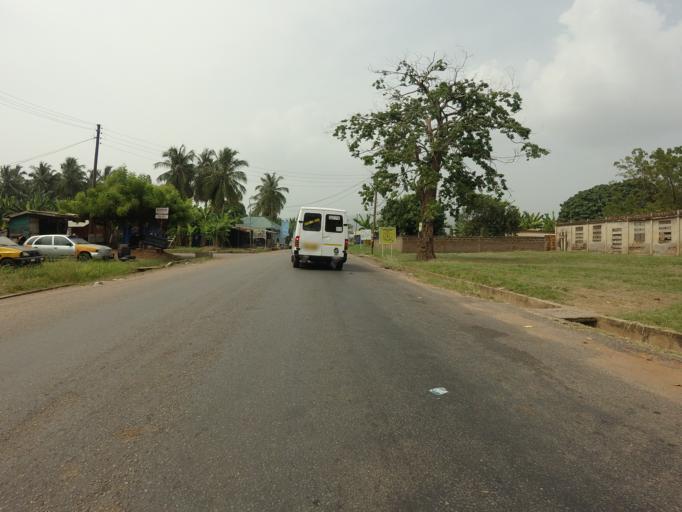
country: GH
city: Akropong
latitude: 6.1029
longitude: -0.0082
